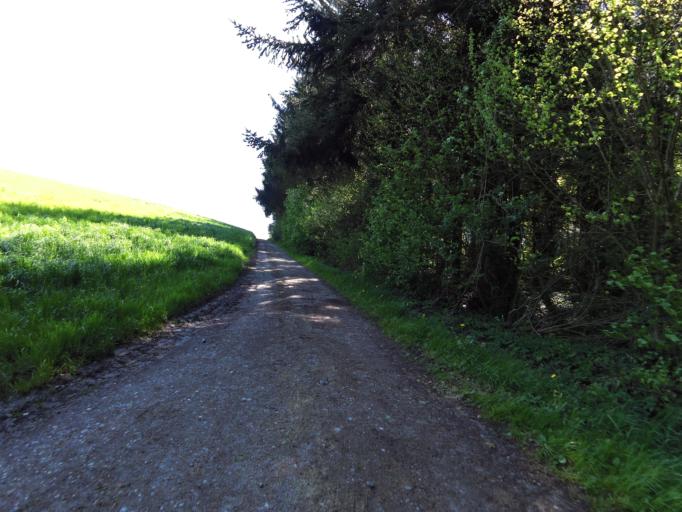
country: CH
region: Thurgau
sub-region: Weinfelden District
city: Weinfelden
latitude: 47.6007
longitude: 9.1039
